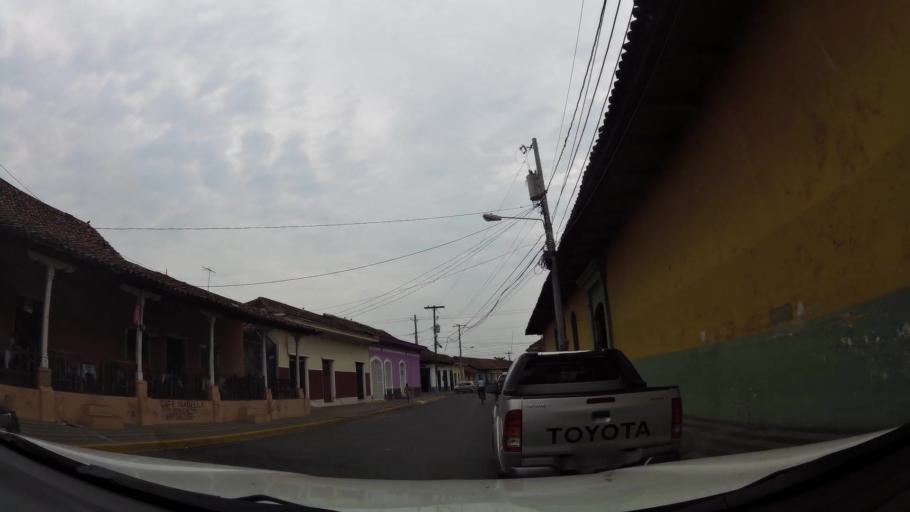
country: NI
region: Granada
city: Granada
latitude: 11.9325
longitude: -85.9558
